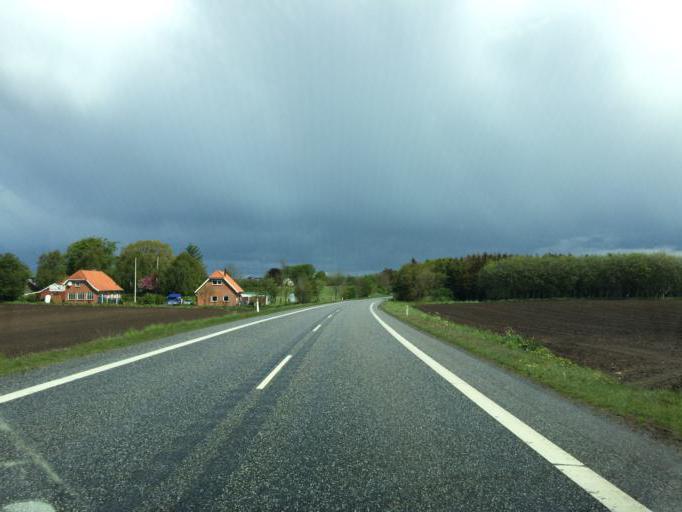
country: DK
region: Central Jutland
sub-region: Skive Kommune
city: Hojslev
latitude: 56.5695
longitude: 9.1181
